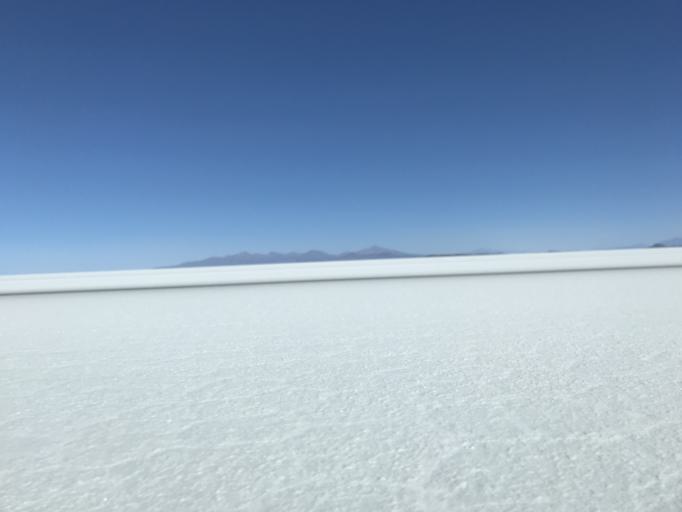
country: BO
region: Potosi
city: Colchani
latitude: -20.2403
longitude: -67.6108
